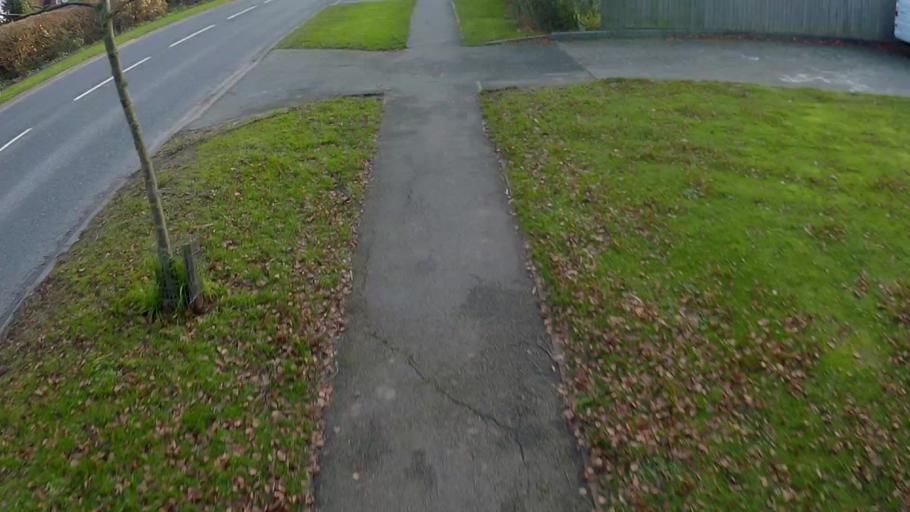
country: GB
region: England
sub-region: Lincolnshire
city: Bourne
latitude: 52.7779
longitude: -0.3762
